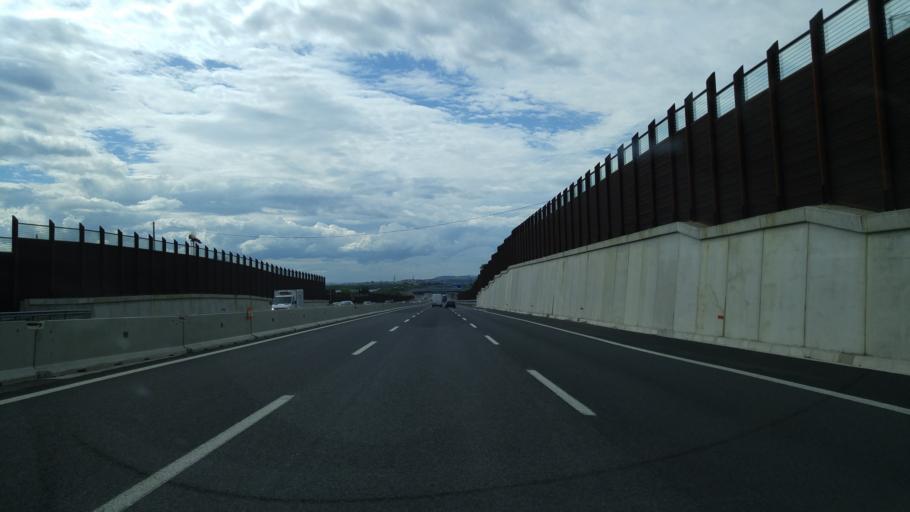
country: IT
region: Emilia-Romagna
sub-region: Provincia di Rimini
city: Riccione
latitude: 43.9818
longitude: 12.6499
